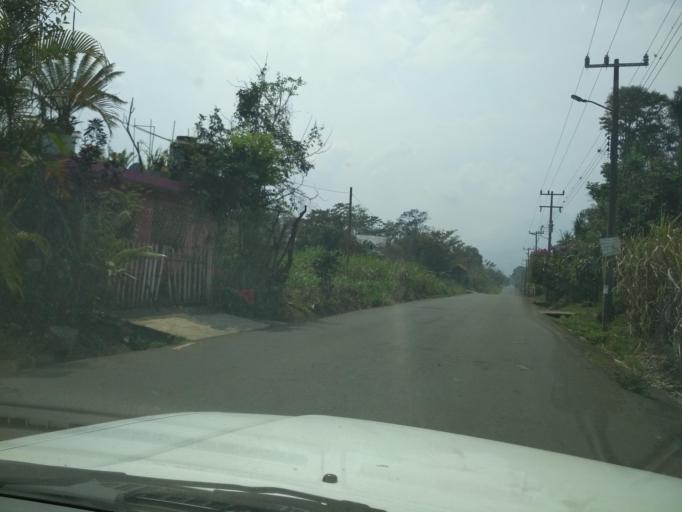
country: MX
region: Veracruz
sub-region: Cordoba
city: Fredepo
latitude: 18.8633
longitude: -96.9843
